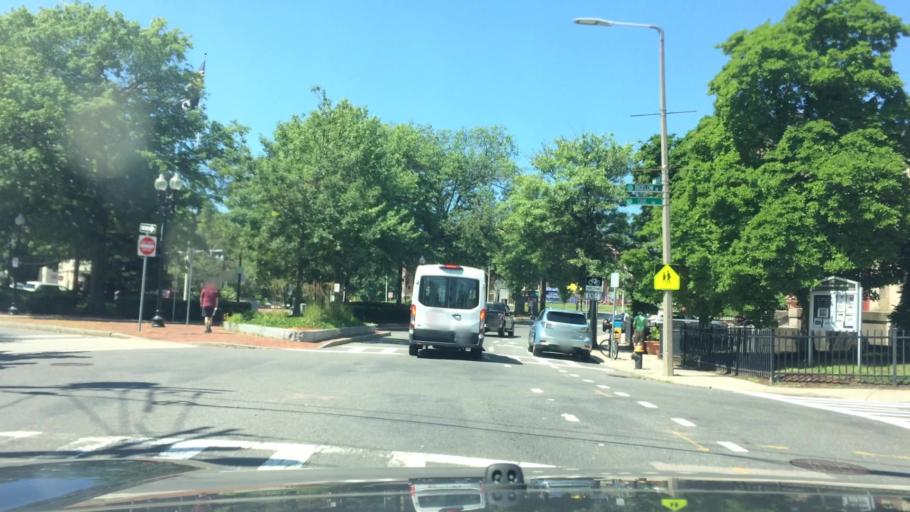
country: US
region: Massachusetts
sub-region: Middlesex County
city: Watertown
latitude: 42.3513
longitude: -71.1674
